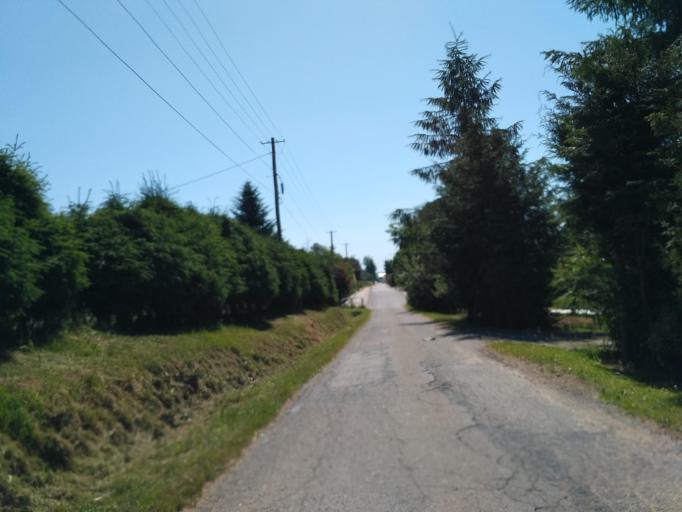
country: PL
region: Subcarpathian Voivodeship
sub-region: Powiat krosnienski
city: Korczyna
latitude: 49.7263
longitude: 21.7827
